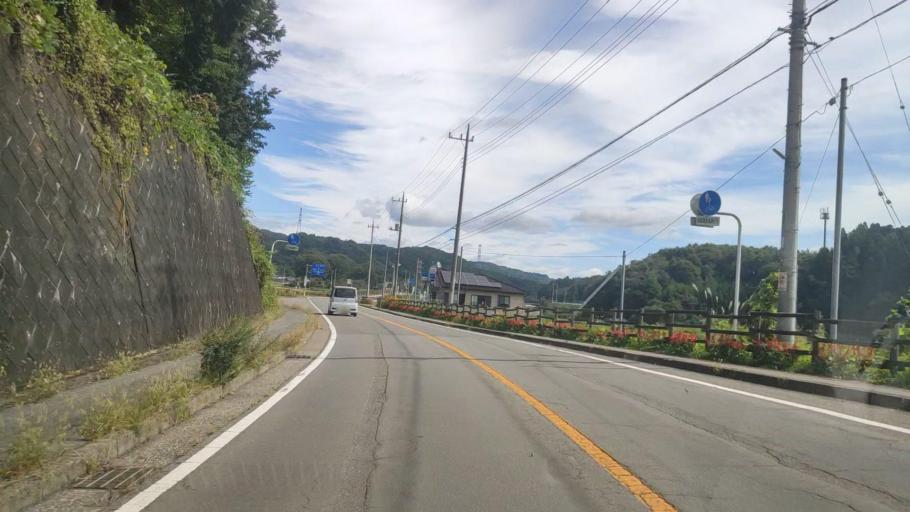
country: JP
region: Gunma
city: Numata
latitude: 36.6247
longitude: 138.9512
